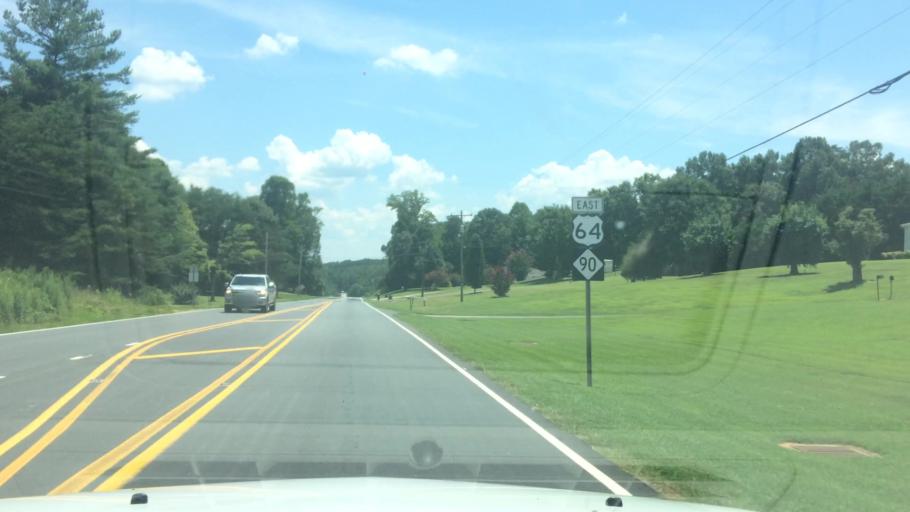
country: US
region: North Carolina
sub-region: Alexander County
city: Taylorsville
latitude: 35.9224
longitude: -81.2605
